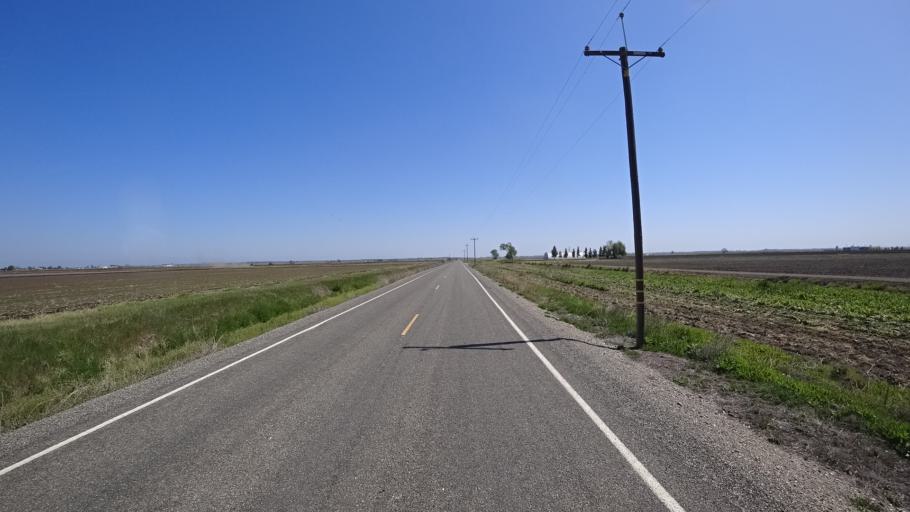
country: US
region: California
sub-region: Glenn County
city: Willows
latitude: 39.5581
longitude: -122.0535
